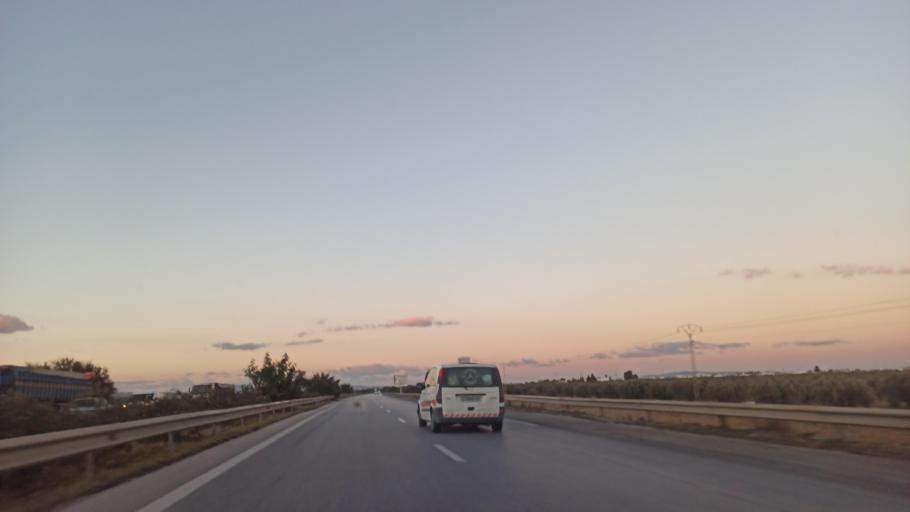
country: TN
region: Nabul
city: Al Hammamat
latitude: 36.2843
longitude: 10.4373
